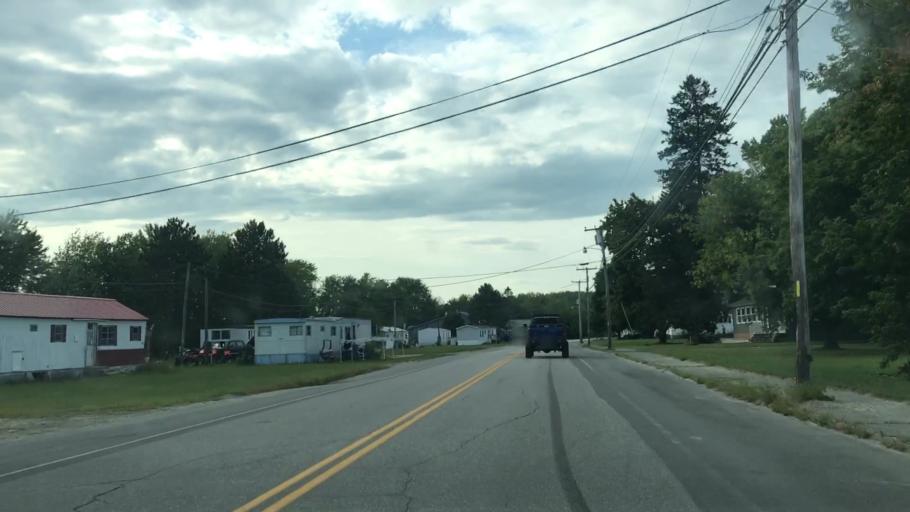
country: US
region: Maine
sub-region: Penobscot County
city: Howland
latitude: 45.2424
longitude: -68.6598
